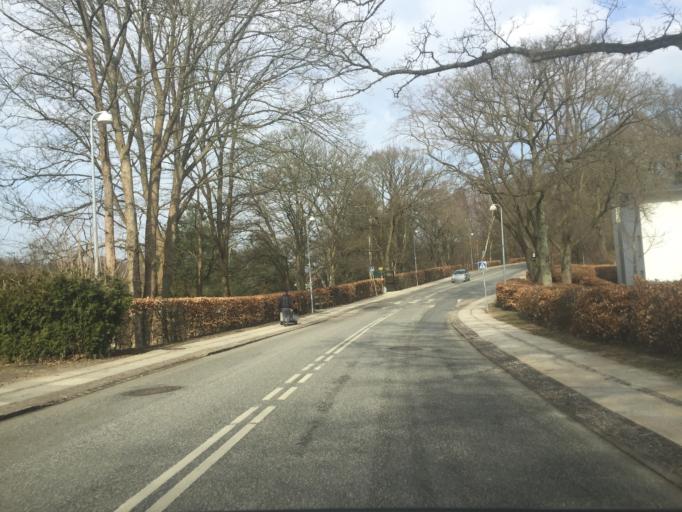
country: DK
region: Capital Region
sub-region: Lyngby-Tarbaek Kommune
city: Kongens Lyngby
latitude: 55.7894
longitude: 12.5024
